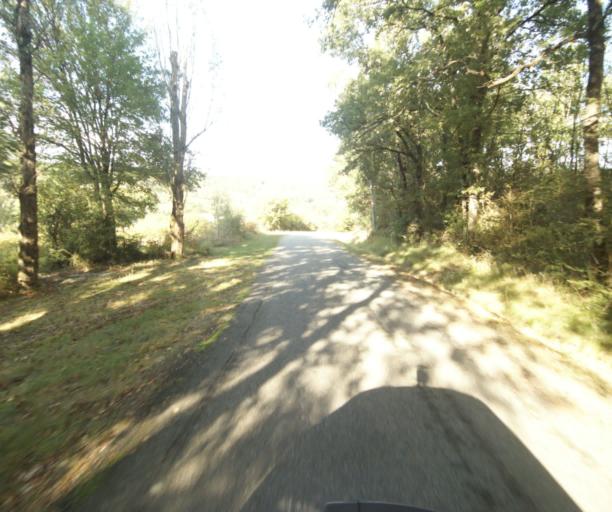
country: FR
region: Midi-Pyrenees
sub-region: Departement du Tarn-et-Garonne
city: Saint-Porquier
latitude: 43.9334
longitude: 1.1442
